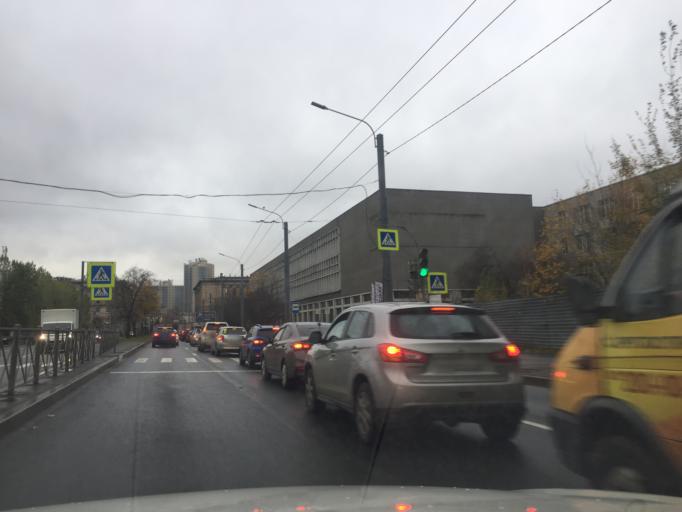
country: RU
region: Leningrad
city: Svetlanovskiy
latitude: 60.0056
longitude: 30.3335
